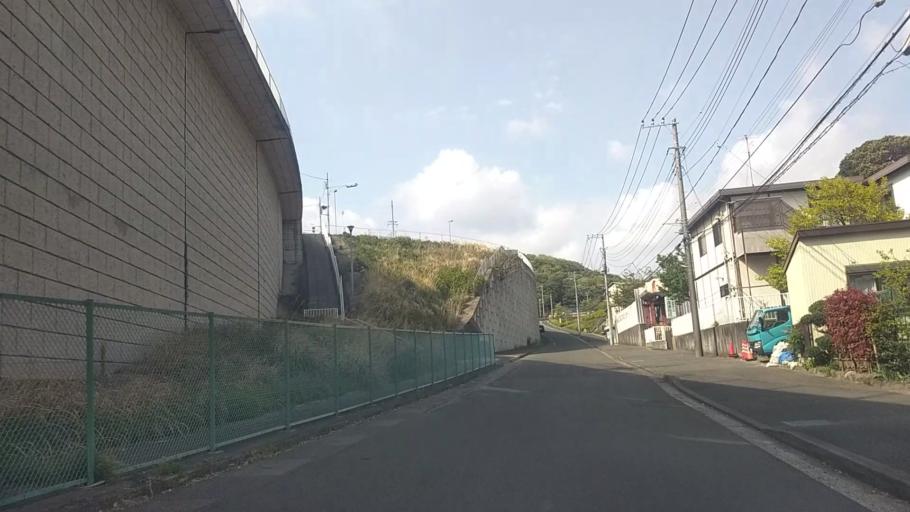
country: JP
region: Kanagawa
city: Kamakura
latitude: 35.3811
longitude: 139.5533
